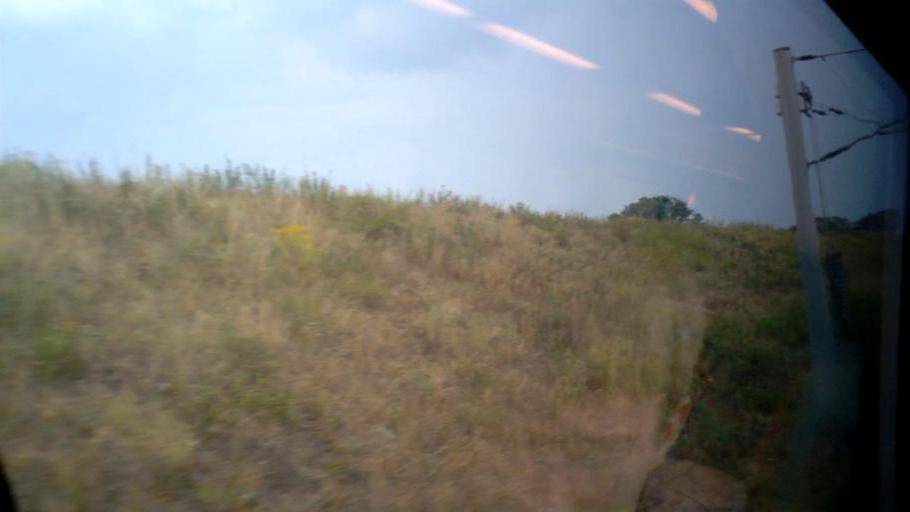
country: DE
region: Brandenburg
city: Grossbeeren
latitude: 52.3442
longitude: 13.2724
